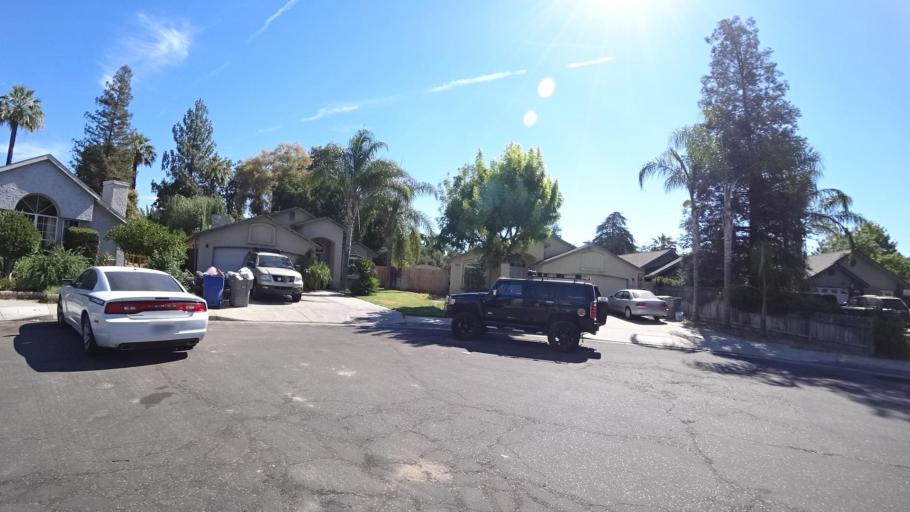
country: US
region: California
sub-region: Fresno County
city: Sunnyside
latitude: 36.7409
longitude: -119.7077
